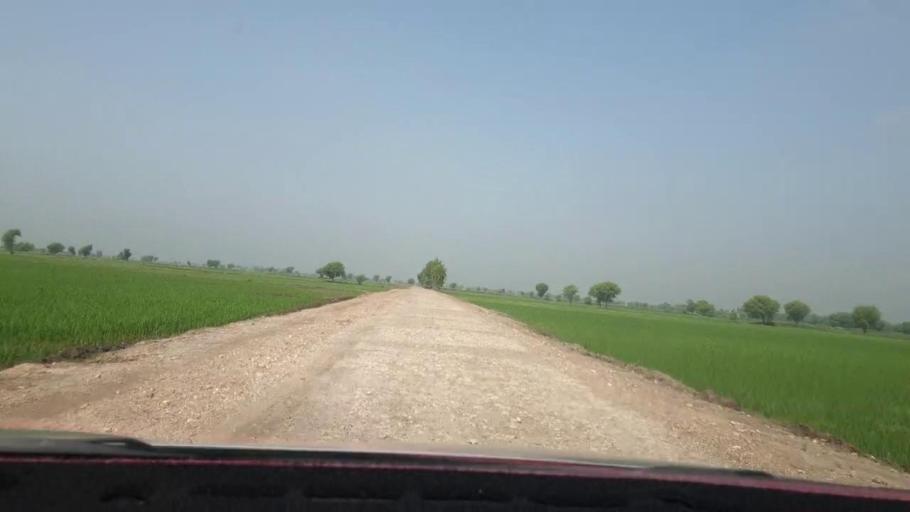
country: PK
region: Sindh
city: Warah
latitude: 27.4303
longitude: 67.8651
